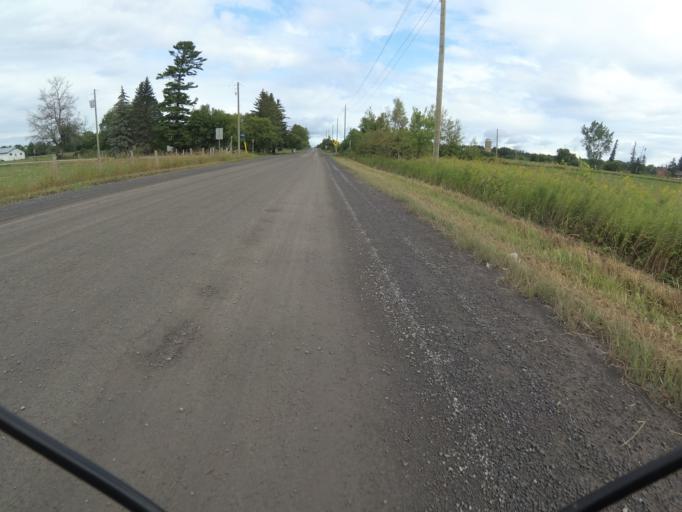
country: CA
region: Ontario
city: Clarence-Rockland
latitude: 45.4742
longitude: -75.3055
